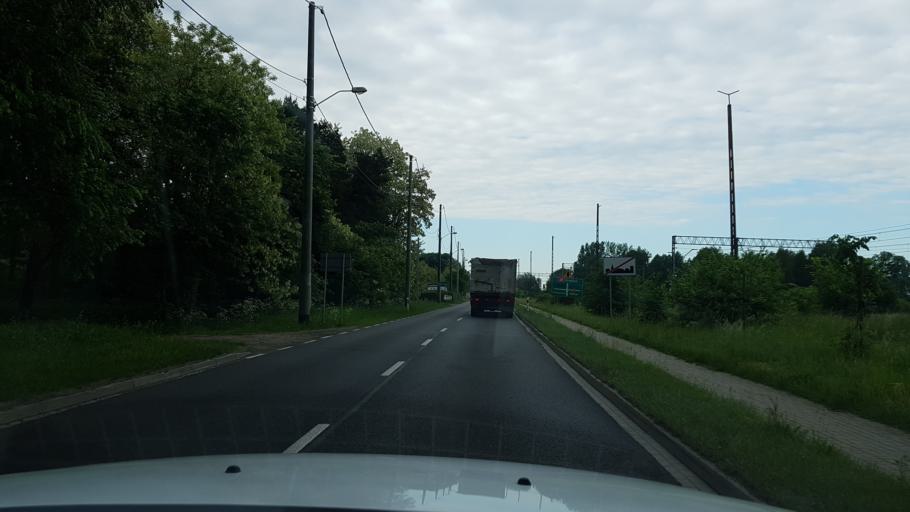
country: PL
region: West Pomeranian Voivodeship
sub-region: Powiat gryfinski
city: Gryfino
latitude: 53.3049
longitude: 14.5289
